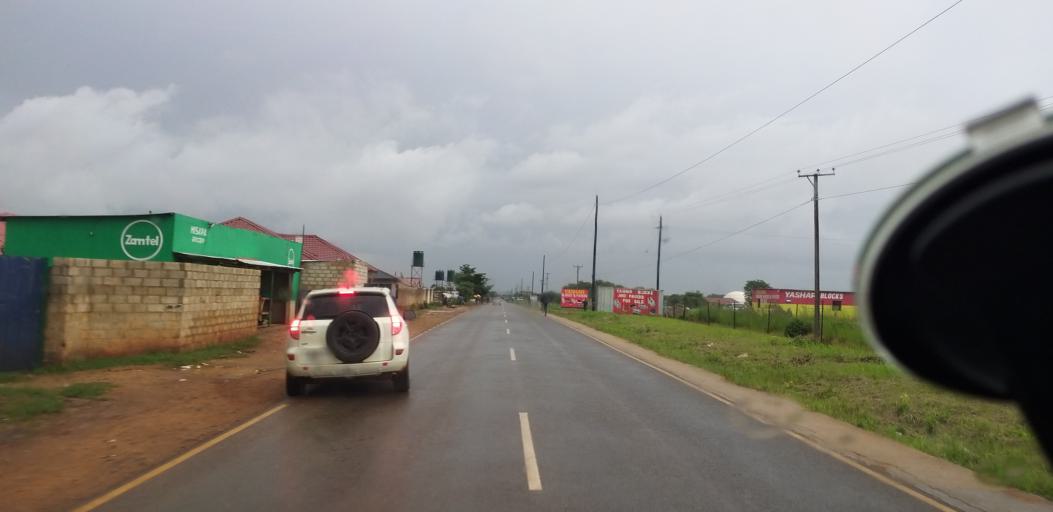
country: ZM
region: Lusaka
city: Lusaka
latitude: -15.5042
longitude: 28.3121
